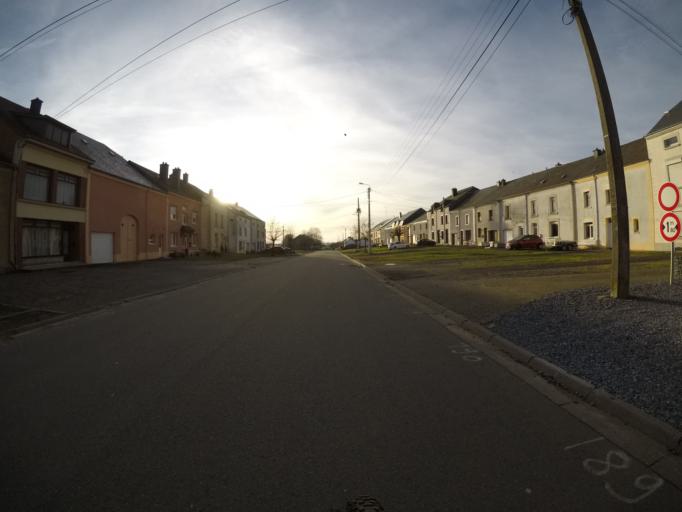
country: BE
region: Wallonia
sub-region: Province du Luxembourg
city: Tintigny
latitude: 49.6763
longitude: 5.4724
